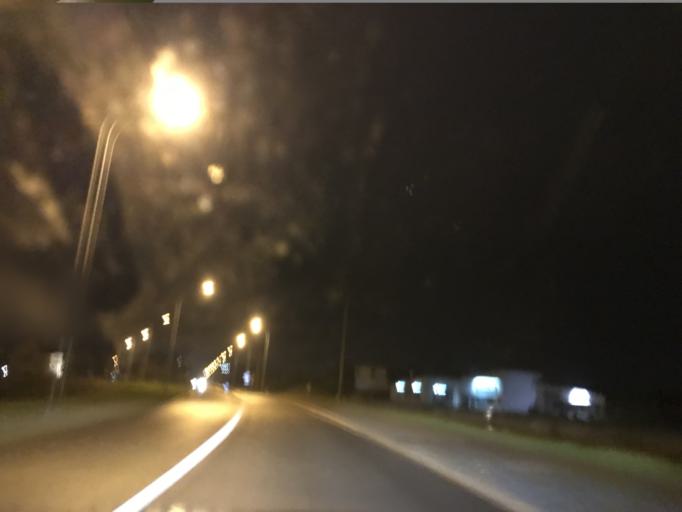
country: FR
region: Auvergne
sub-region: Departement de l'Allier
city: Vichy
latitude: 46.1081
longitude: 3.4223
